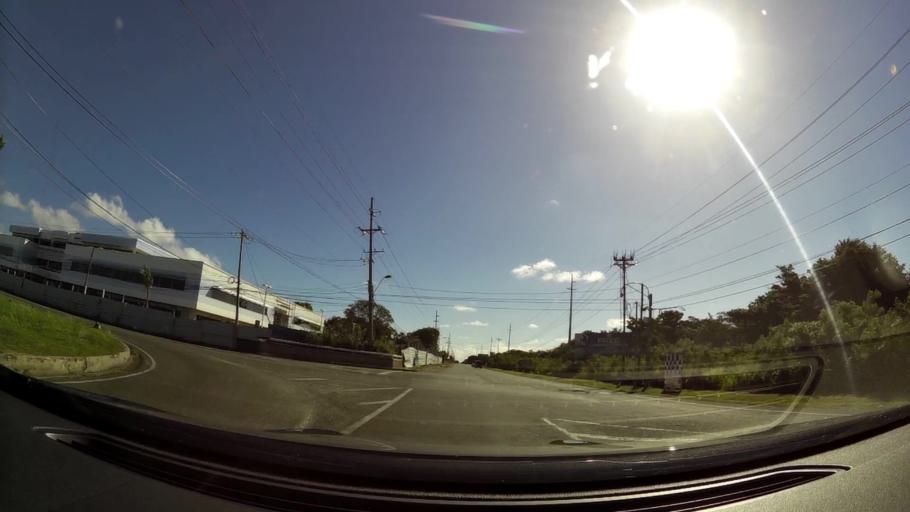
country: TT
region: Tobago
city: Scarborough
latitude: 11.1558
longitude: -60.8002
